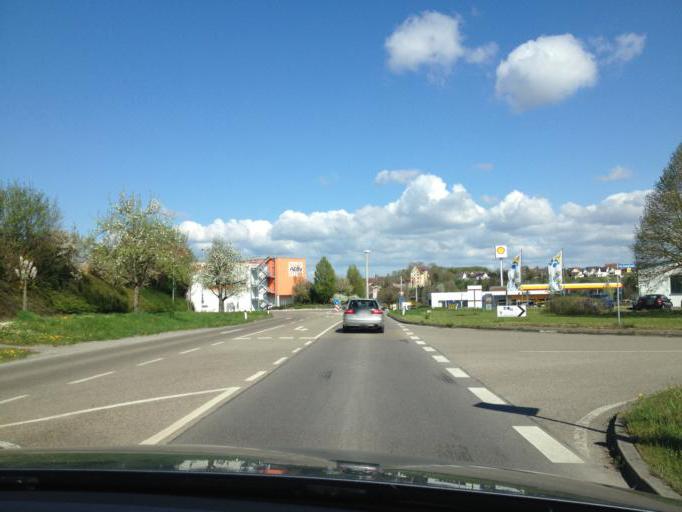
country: DE
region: Baden-Wuerttemberg
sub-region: Regierungsbezirk Stuttgart
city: Neuenstadt am Kocher
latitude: 49.2366
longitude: 9.3434
